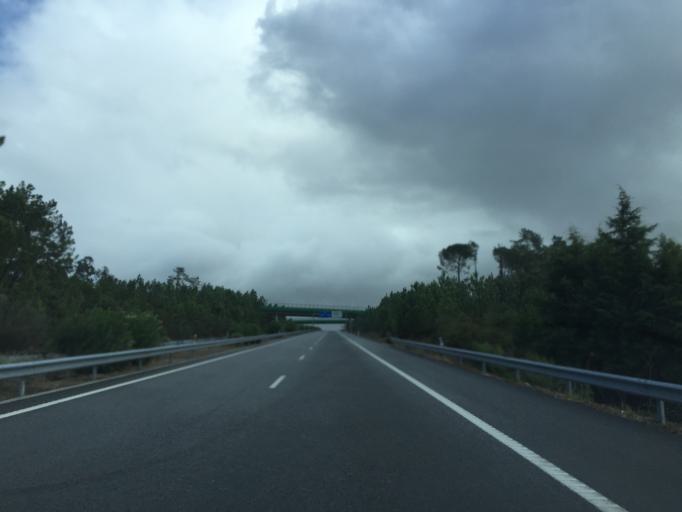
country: PT
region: Coimbra
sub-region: Cantanhede
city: Cantanhede
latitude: 40.2844
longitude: -8.5345
